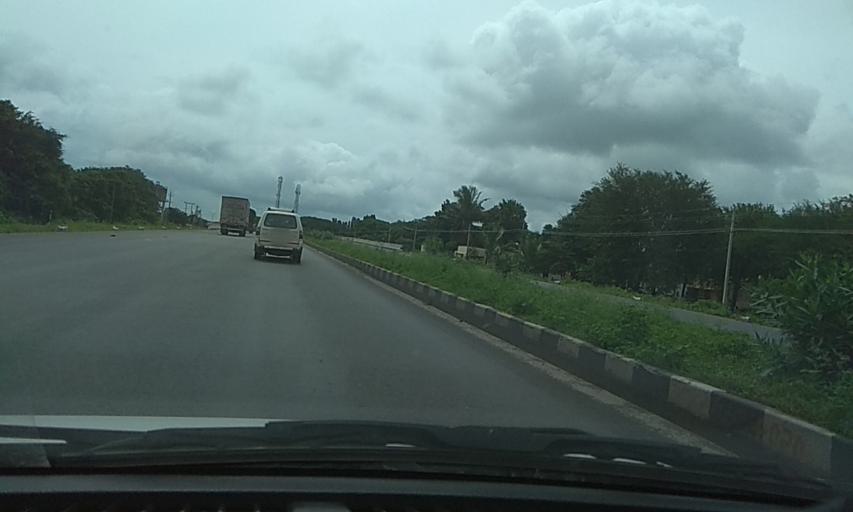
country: IN
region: Karnataka
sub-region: Davanagere
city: Mayakonda
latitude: 14.3787
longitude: 76.0944
